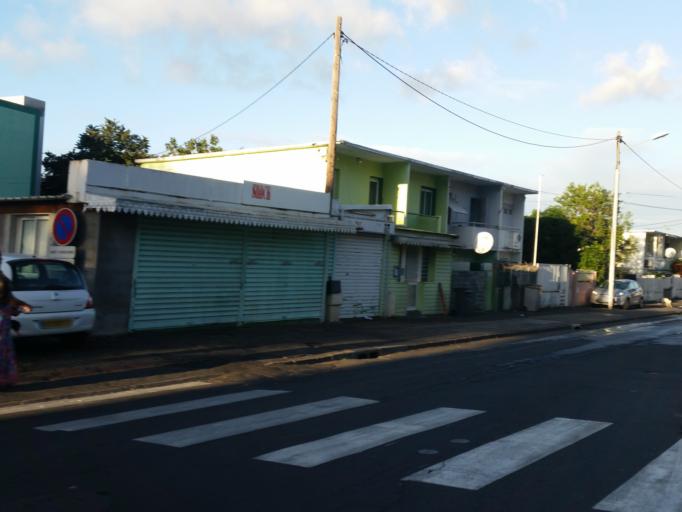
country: RE
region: Reunion
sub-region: Reunion
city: Saint-Denis
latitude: -20.8906
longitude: 55.4482
